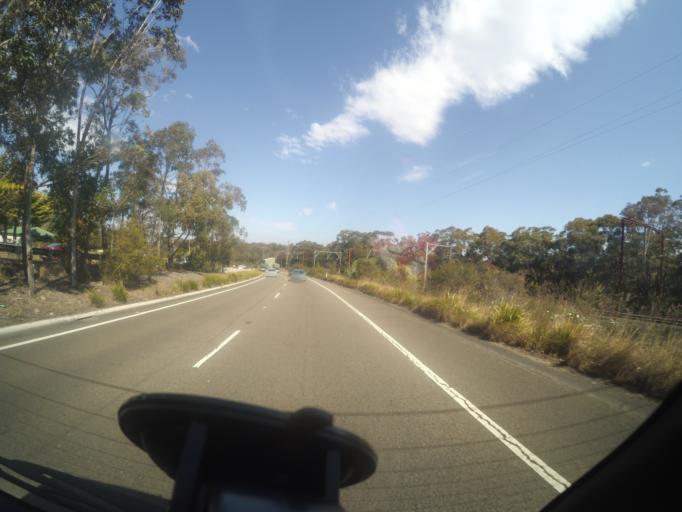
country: AU
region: New South Wales
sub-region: Blue Mountains Municipality
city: Blaxland
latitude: -33.7169
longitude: 150.5932
